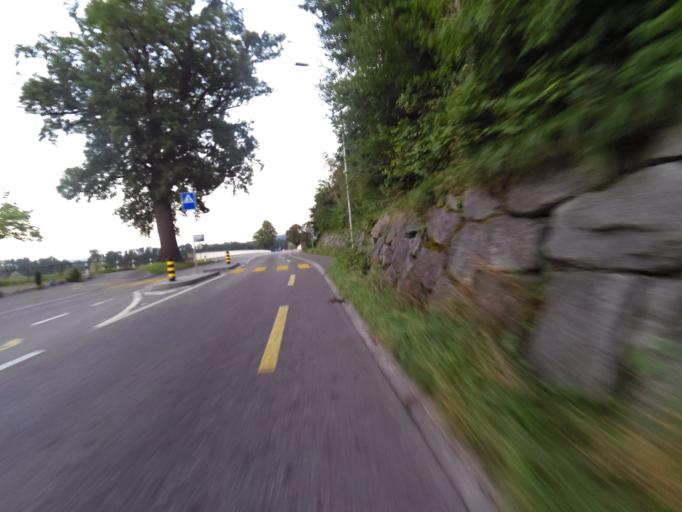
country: CH
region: Thurgau
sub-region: Weinfelden District
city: Maerstetten-Dorf
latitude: 47.5712
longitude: 9.0602
